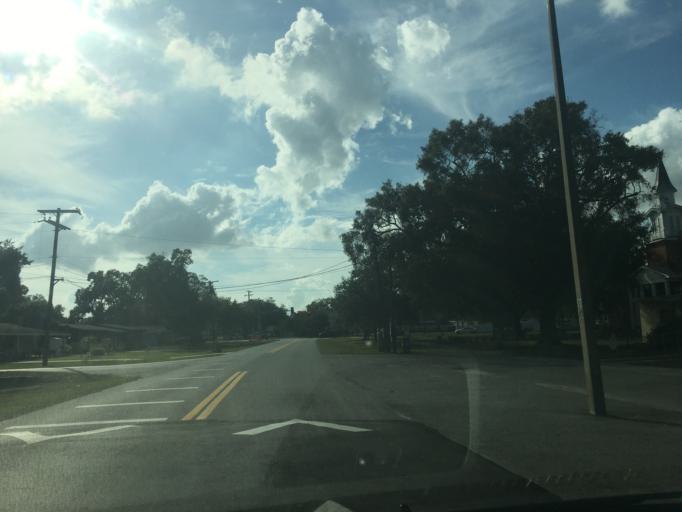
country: US
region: Florida
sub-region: Hillsborough County
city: Egypt Lake-Leto
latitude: 27.9901
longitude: -82.4751
